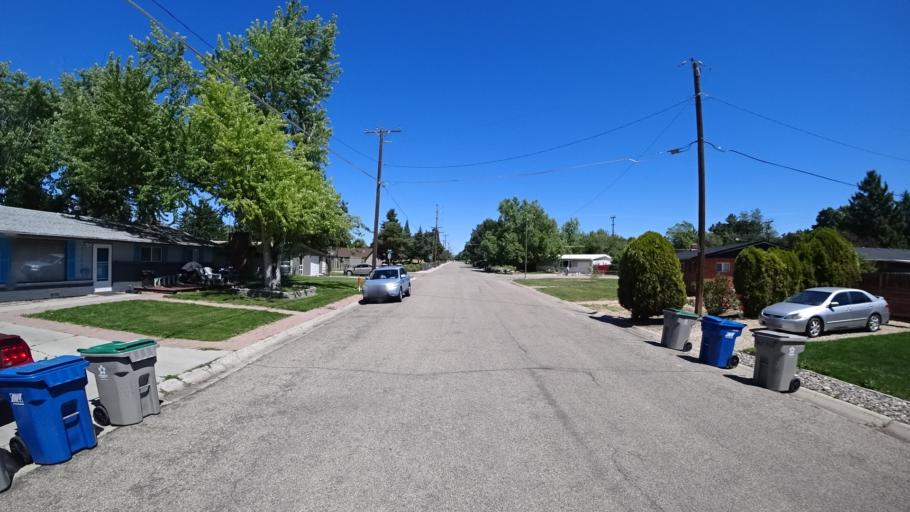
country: US
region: Idaho
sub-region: Ada County
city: Garden City
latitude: 43.5743
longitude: -116.2336
